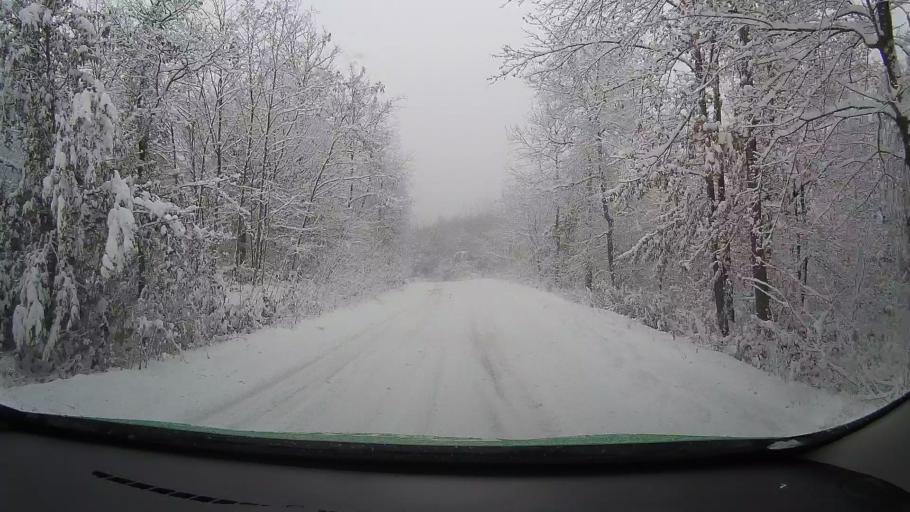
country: RO
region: Hunedoara
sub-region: Comuna Teliucu Inferior
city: Teliucu Inferior
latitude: 45.6890
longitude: 22.8982
